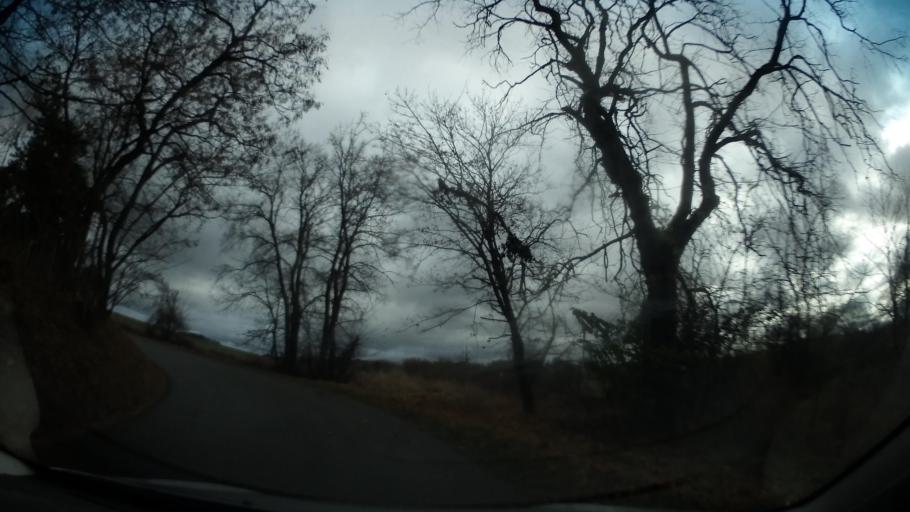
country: CZ
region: Vysocina
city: Namest' nad Oslavou
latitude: 49.2851
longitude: 16.1058
